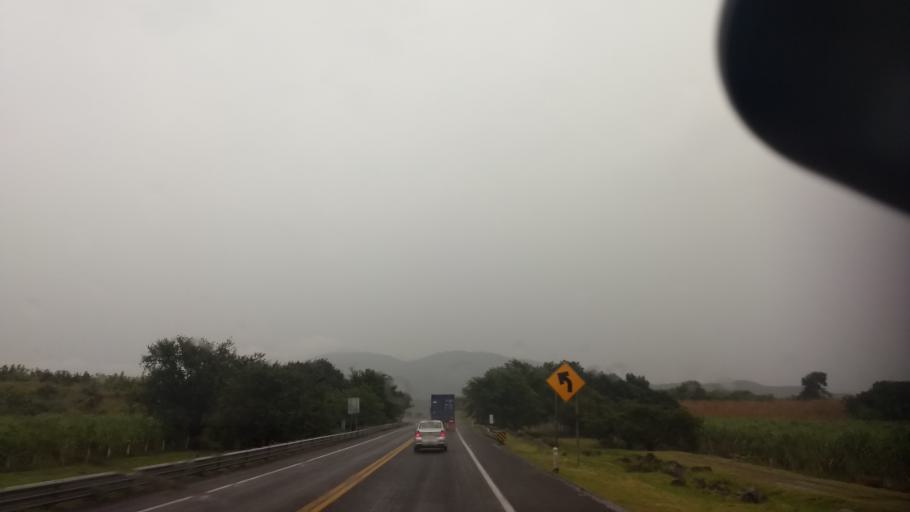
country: MX
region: Jalisco
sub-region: Tonila
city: San Marcos
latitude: 19.4346
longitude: -103.4861
